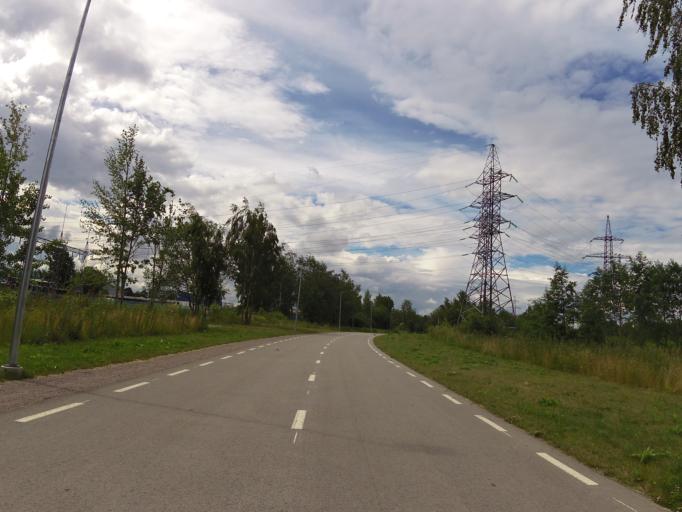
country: EE
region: Harju
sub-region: Tallinna linn
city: Tallinn
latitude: 59.4173
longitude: 24.6709
